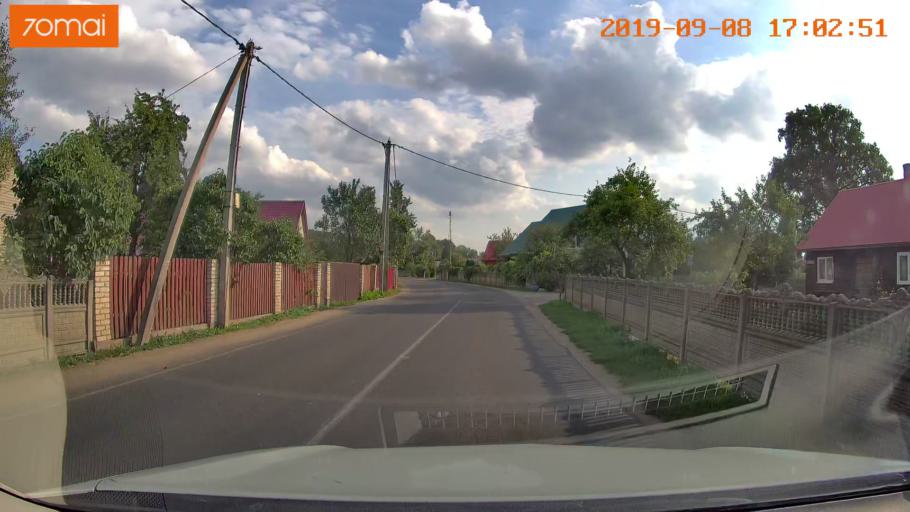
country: BY
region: Grodnenskaya
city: Hrodna
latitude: 53.6998
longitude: 23.9404
